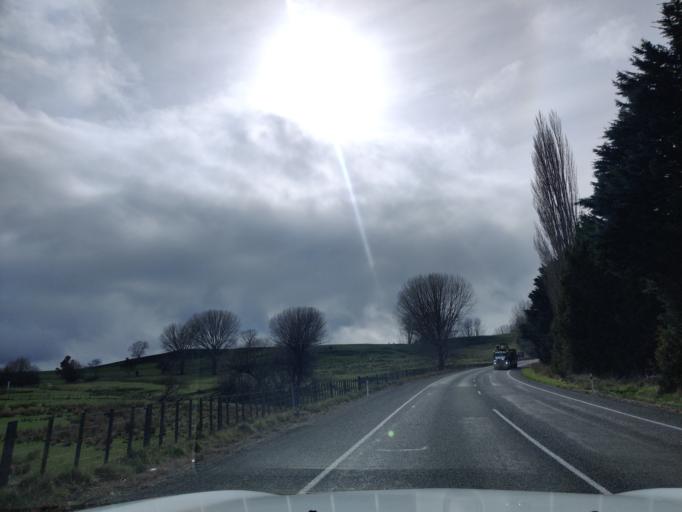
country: NZ
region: Manawatu-Wanganui
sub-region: Ruapehu District
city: Waiouru
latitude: -39.7428
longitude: 175.8357
